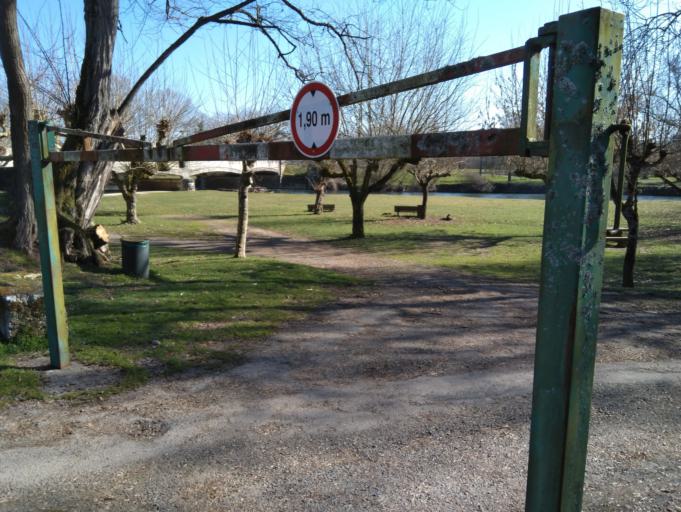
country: FR
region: Midi-Pyrenees
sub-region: Departement du Gers
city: Riscle
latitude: 43.6406
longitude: -0.0212
